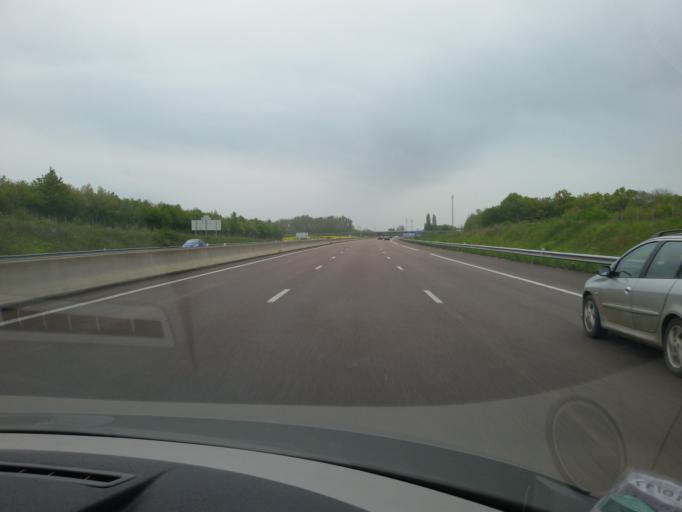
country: FR
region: Bourgogne
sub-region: Departement de la Cote-d'Or
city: Gevrey-Chambertin
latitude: 47.2049
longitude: 4.9974
